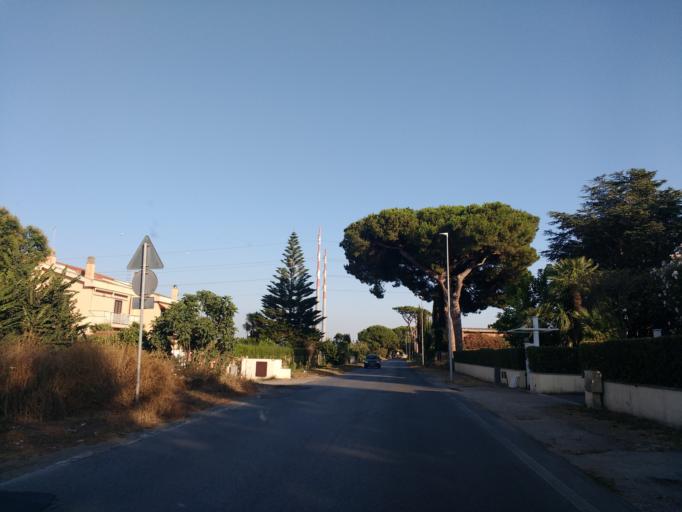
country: IT
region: Latium
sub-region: Citta metropolitana di Roma Capitale
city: Fregene
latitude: 41.8568
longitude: 12.2161
